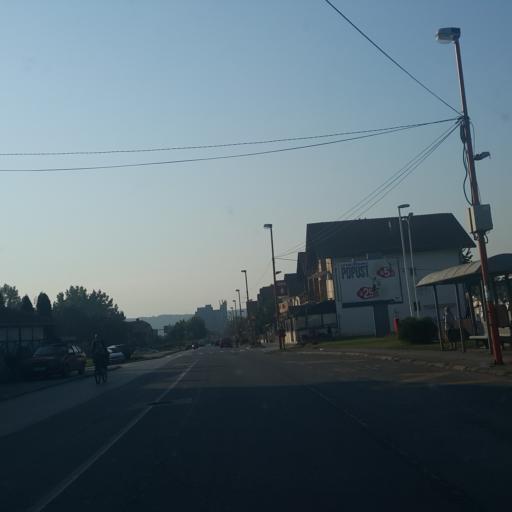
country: RS
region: Central Serbia
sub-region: Zajecarski Okrug
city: Zajecar
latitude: 43.9110
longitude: 22.2603
